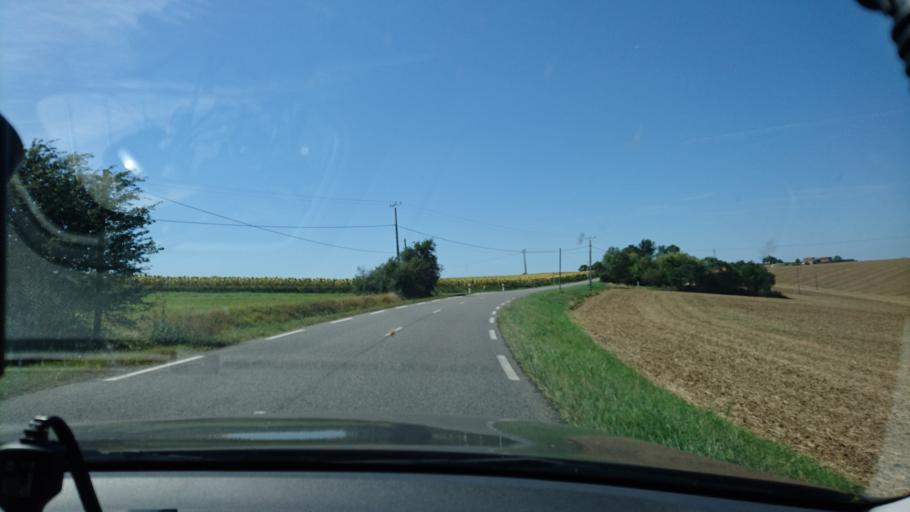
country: FR
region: Midi-Pyrenees
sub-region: Departement de la Haute-Garonne
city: Saint-Sulpice-sur-Leze
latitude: 43.3326
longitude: 1.2984
